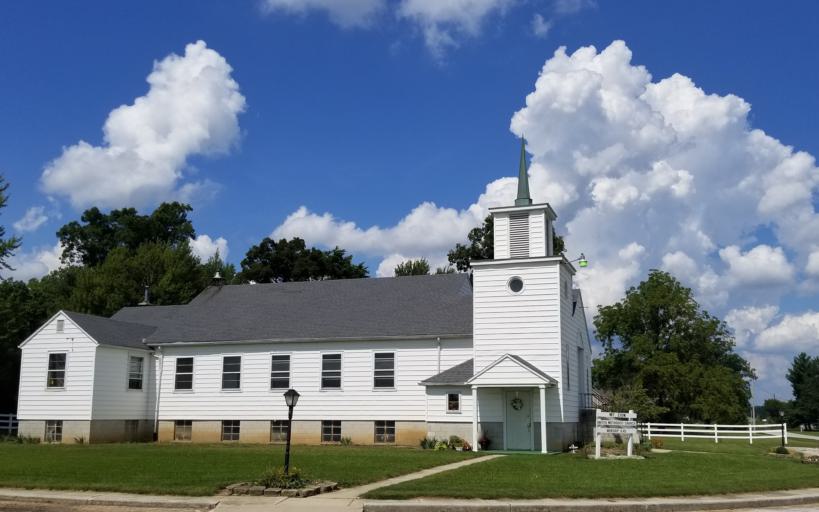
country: US
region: Ohio
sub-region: Hancock County
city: Arlington
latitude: 40.8627
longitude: -83.5999
